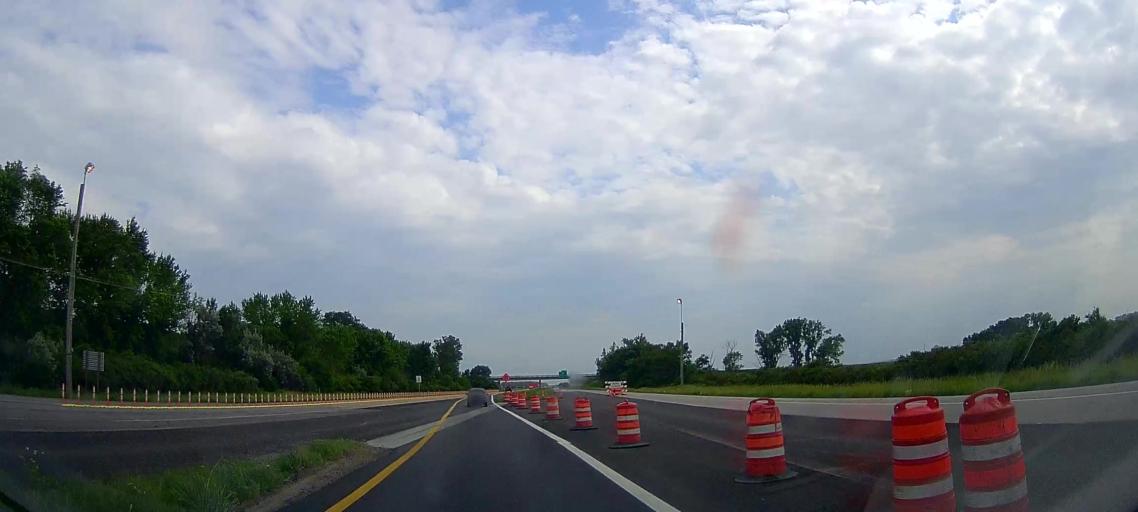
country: US
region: Nebraska
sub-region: Burt County
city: Tekamah
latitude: 41.7320
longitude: -96.0479
